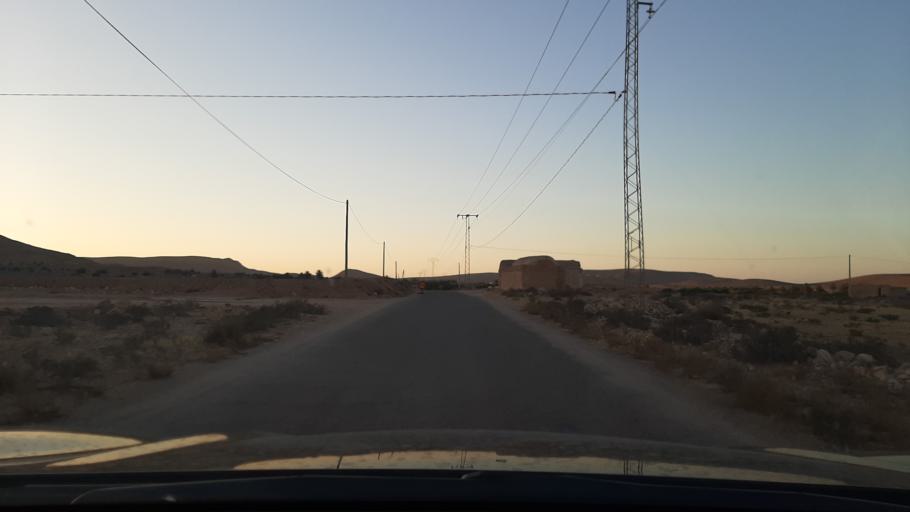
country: TN
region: Qabis
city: Matmata
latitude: 33.5501
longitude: 10.1887
